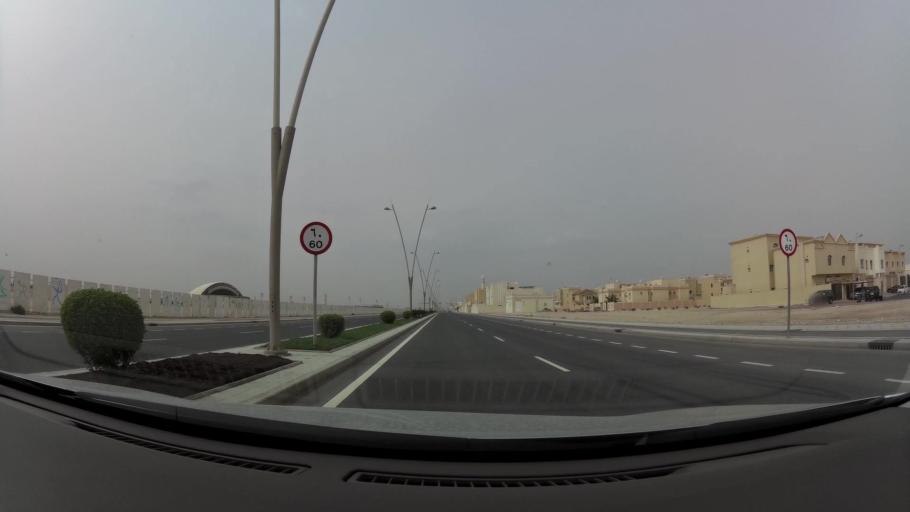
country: QA
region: Baladiyat ad Dawhah
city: Doha
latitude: 25.2265
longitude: 51.5360
